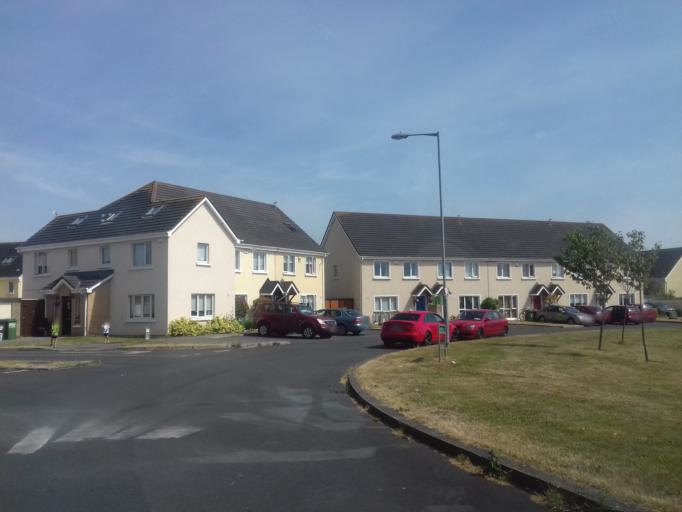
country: IE
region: Leinster
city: Lusk
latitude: 53.5233
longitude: -6.1727
